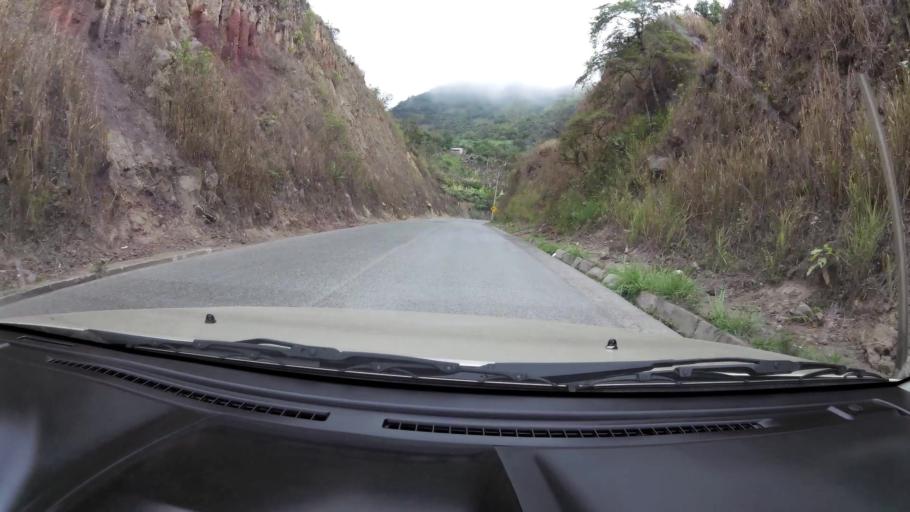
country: EC
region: El Oro
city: Pasaje
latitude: -3.3059
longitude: -79.5305
